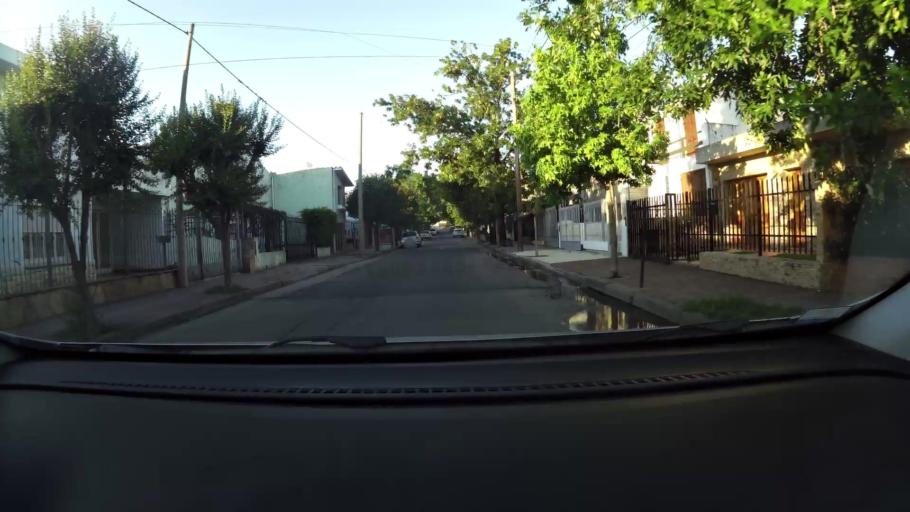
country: AR
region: Cordoba
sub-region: Departamento de Capital
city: Cordoba
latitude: -31.3857
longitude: -64.2102
